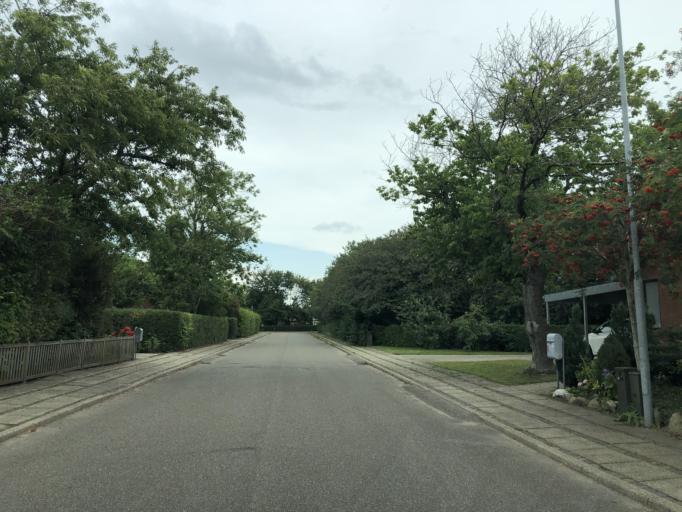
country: DK
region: Central Jutland
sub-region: Ringkobing-Skjern Kommune
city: Ringkobing
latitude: 56.0948
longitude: 8.2638
